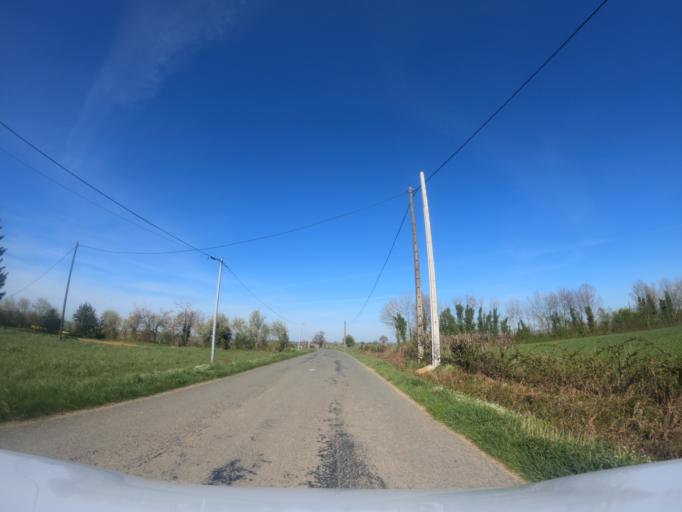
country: FR
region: Pays de la Loire
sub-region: Departement de la Vendee
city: Saint-Pierre-du-Chemin
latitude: 46.7048
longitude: -0.7411
